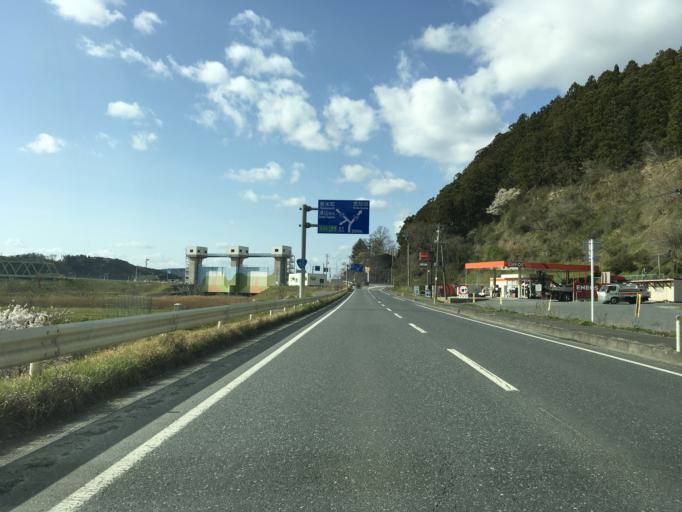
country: JP
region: Miyagi
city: Wakuya
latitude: 38.6011
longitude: 141.3030
